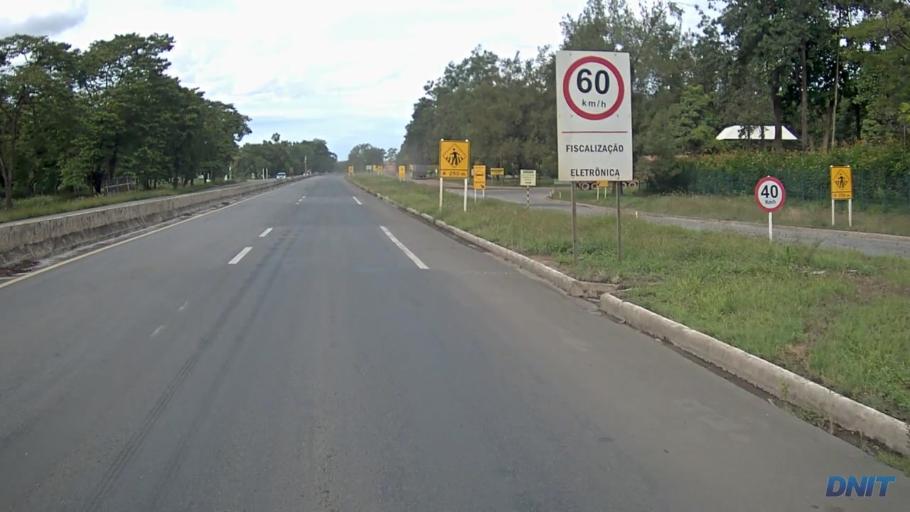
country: BR
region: Minas Gerais
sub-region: Ipaba
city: Ipaba
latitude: -19.3158
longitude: -42.3997
